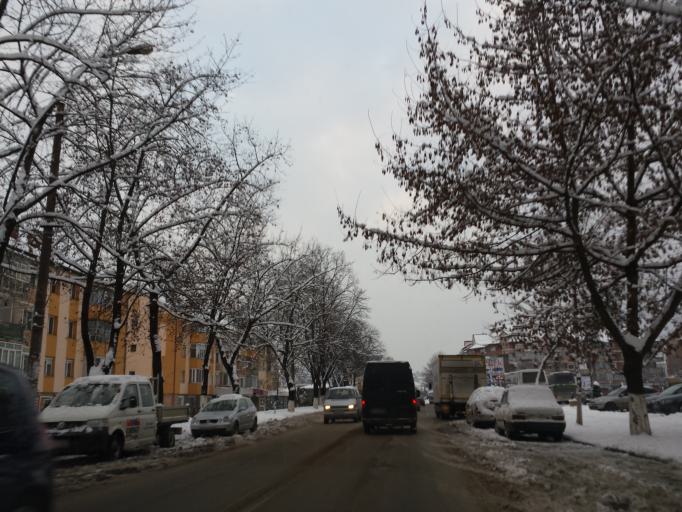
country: RO
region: Hunedoara
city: Hunedoara
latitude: 45.7561
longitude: 22.9010
